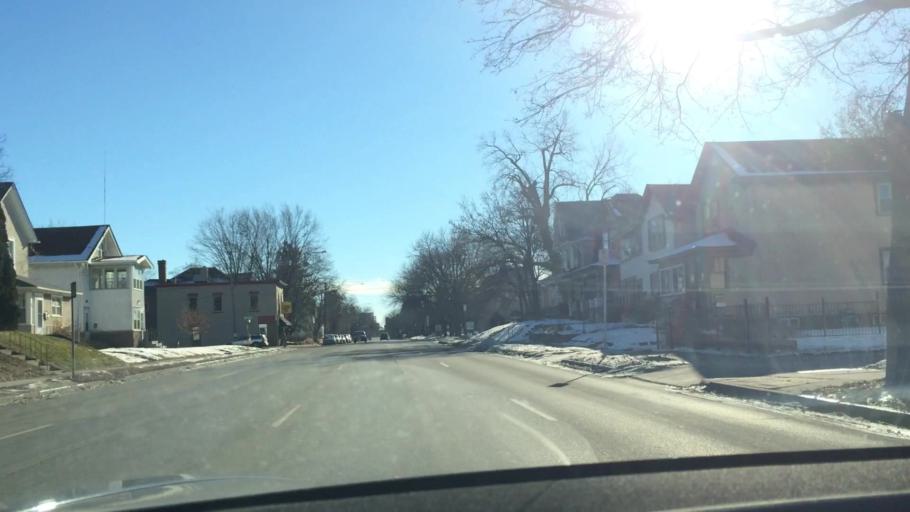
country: US
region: Minnesota
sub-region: Hennepin County
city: Minneapolis
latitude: 44.9963
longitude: -93.2621
